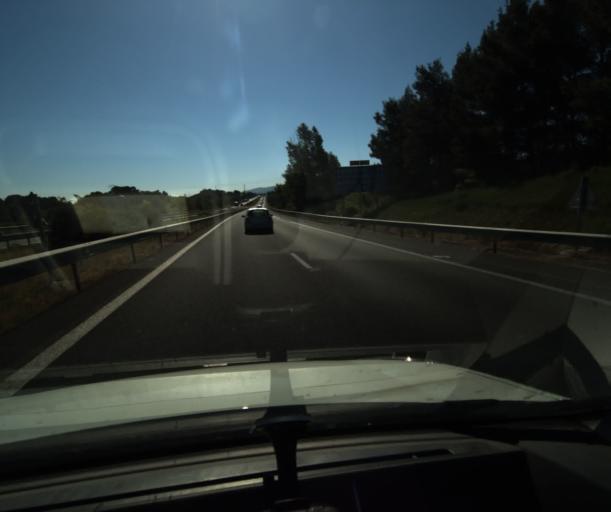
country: FR
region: Languedoc-Roussillon
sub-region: Departement de l'Aude
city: Trebes
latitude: 43.1965
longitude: 2.4326
